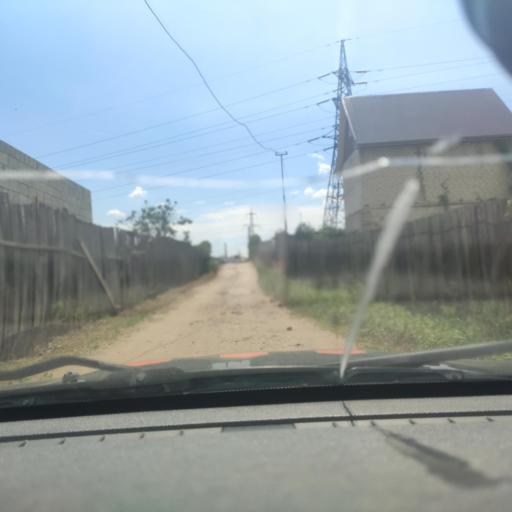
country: RU
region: Samara
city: Zhigulevsk
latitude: 53.5005
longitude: 49.4947
